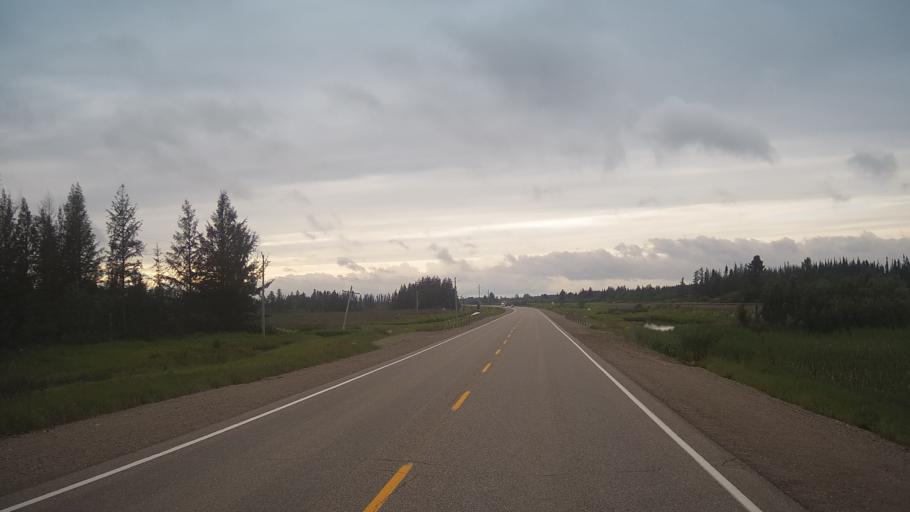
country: CA
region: Ontario
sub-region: Thunder Bay District
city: Thunder Bay
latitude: 48.8711
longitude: -89.9760
